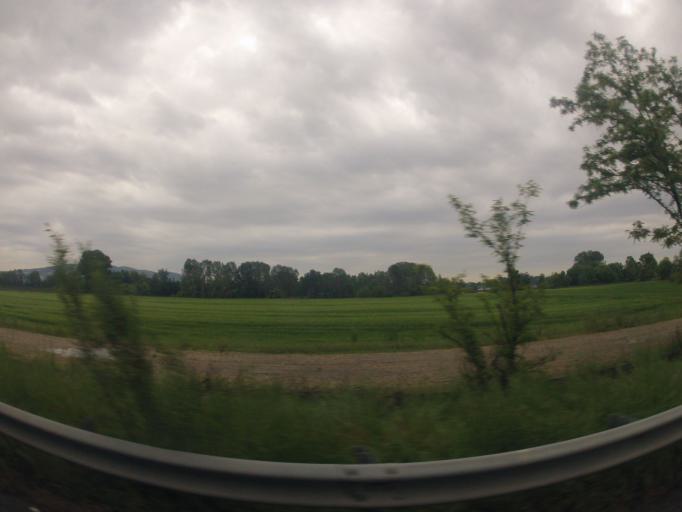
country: IT
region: Piedmont
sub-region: Provincia di Torino
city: La Loggia
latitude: 44.9616
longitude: 7.6791
